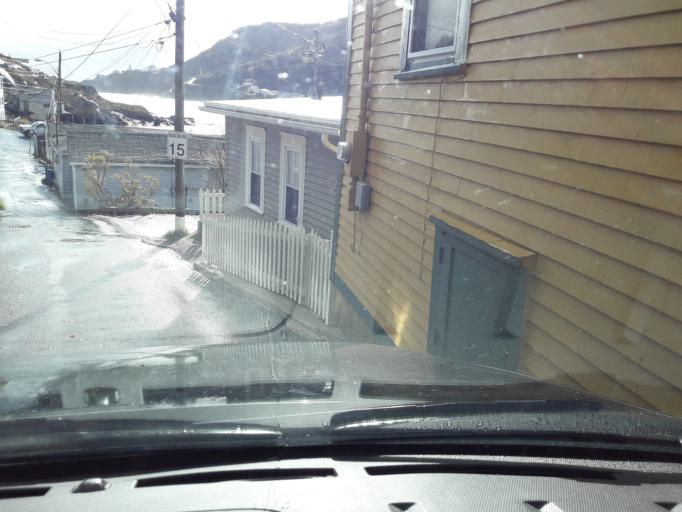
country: CA
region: Newfoundland and Labrador
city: St. John's
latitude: 47.5686
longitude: -52.6898
